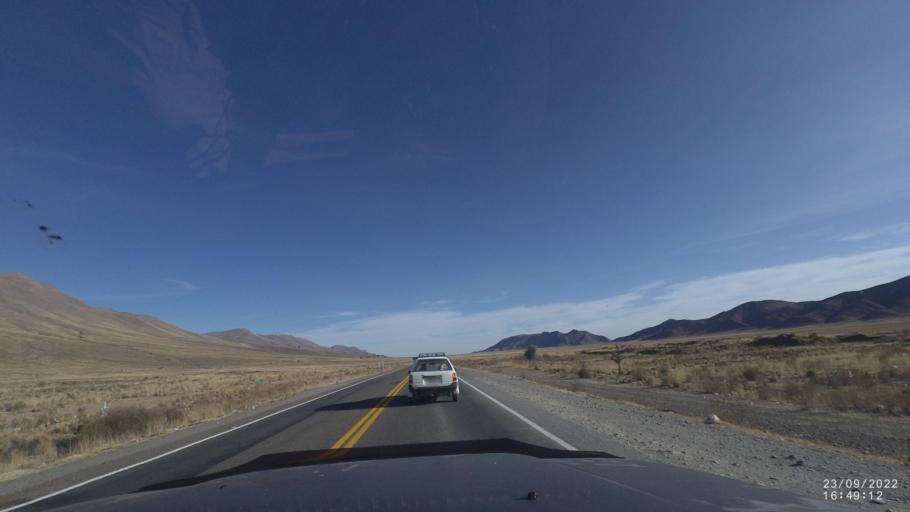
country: BO
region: Oruro
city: Poopo
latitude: -18.3864
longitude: -66.9789
